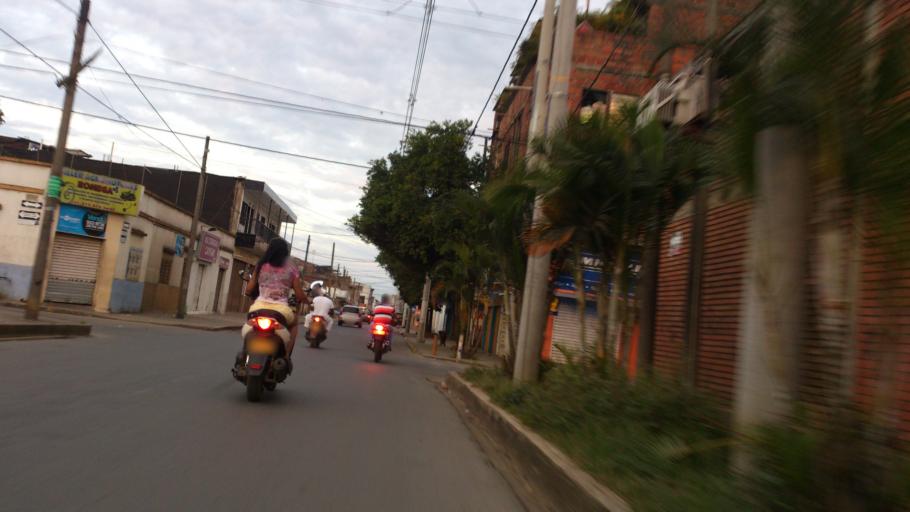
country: CO
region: Valle del Cauca
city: Jamundi
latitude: 3.2588
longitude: -76.5436
